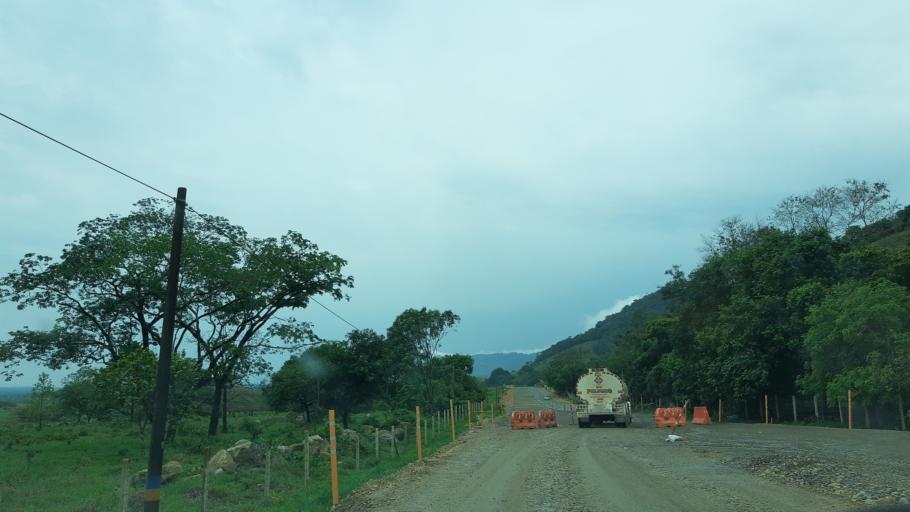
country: CO
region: Casanare
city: Sabanalarga
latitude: 4.8214
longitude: -72.9687
